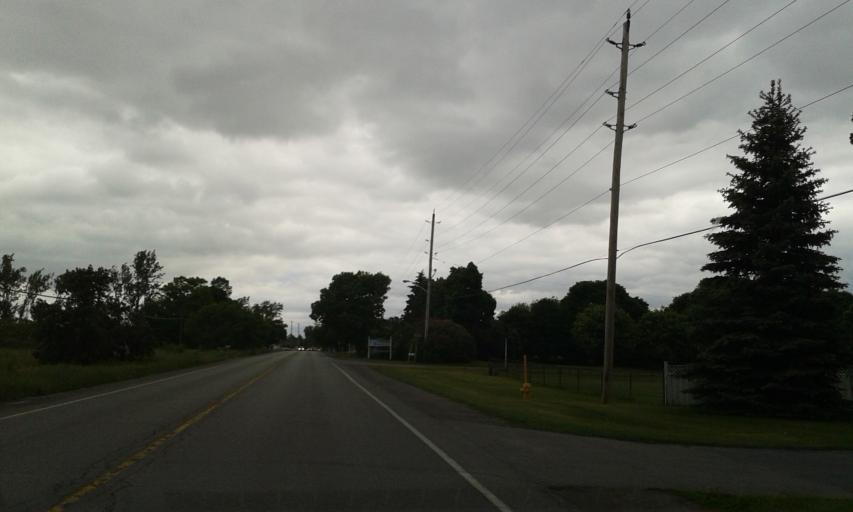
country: CA
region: Ontario
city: Prince Edward
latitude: 43.9469
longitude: -77.3709
